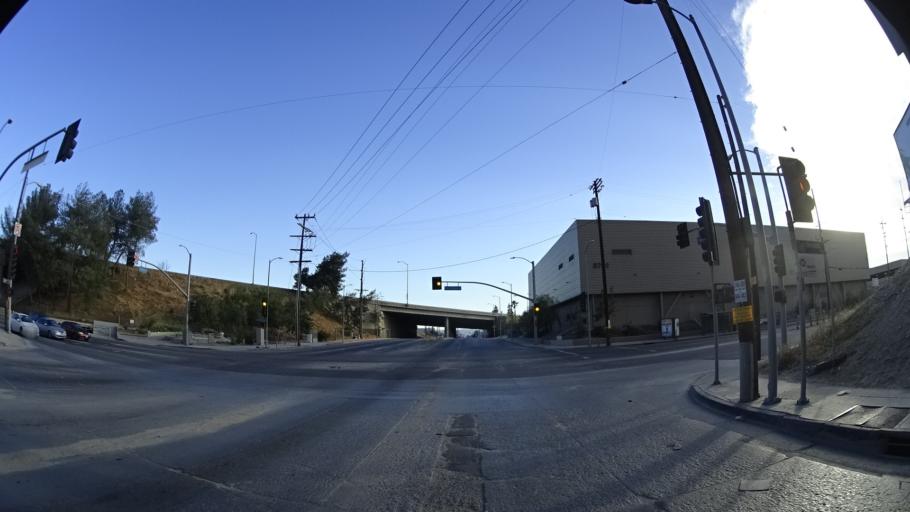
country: US
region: California
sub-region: Los Angeles County
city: North Hollywood
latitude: 34.2277
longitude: -118.3808
